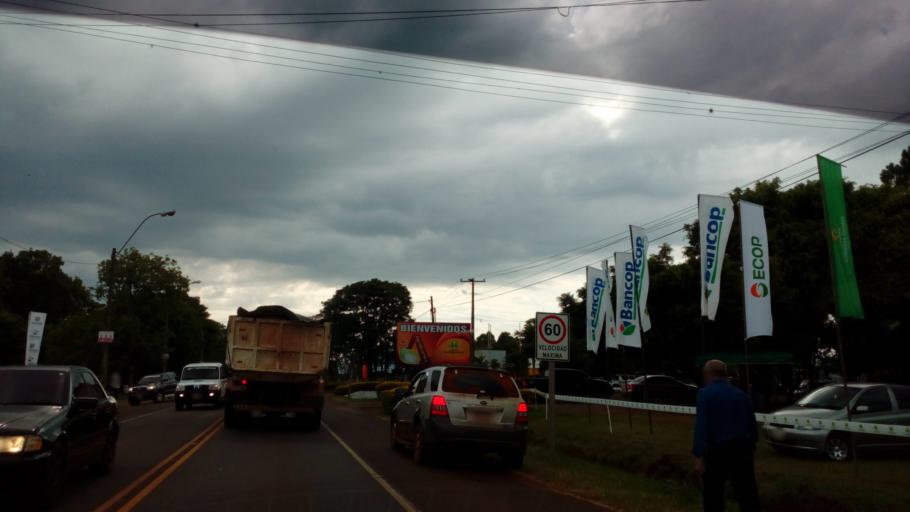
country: PY
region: Itapua
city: Obligado
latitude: -27.0722
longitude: -55.6328
